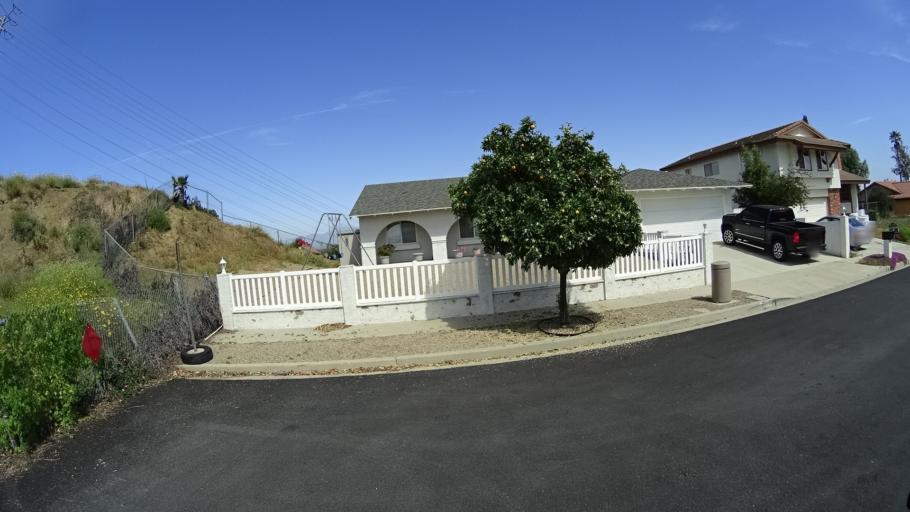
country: US
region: California
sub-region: Ventura County
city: Moorpark
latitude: 34.2324
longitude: -118.8658
